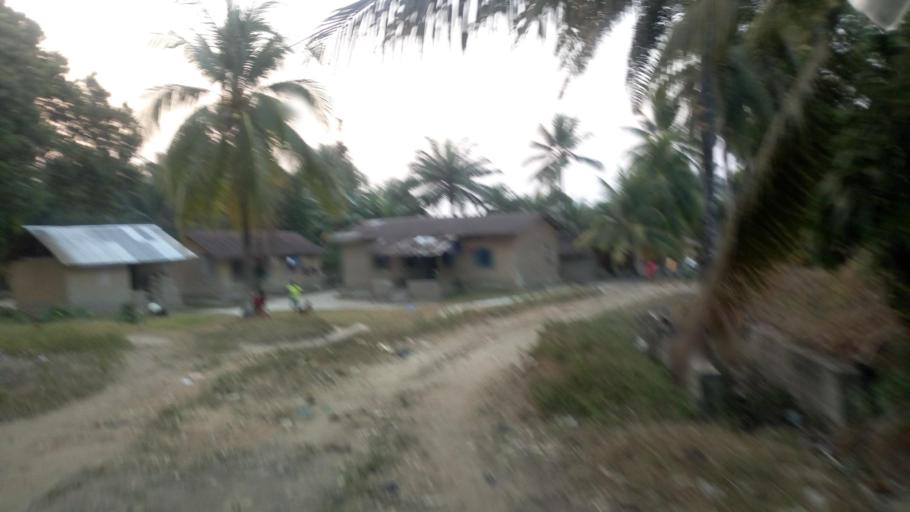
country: SL
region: Southern Province
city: Mogbwemo
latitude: 7.6072
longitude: -12.1722
